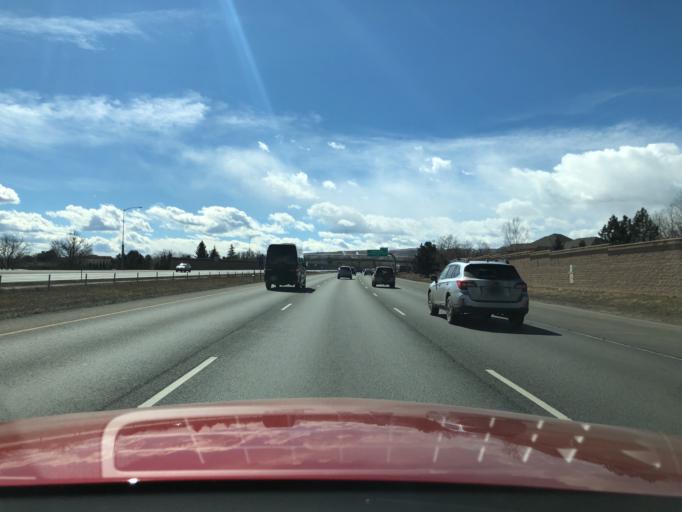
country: US
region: Colorado
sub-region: Jefferson County
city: Applewood
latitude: 39.7577
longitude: -105.1441
